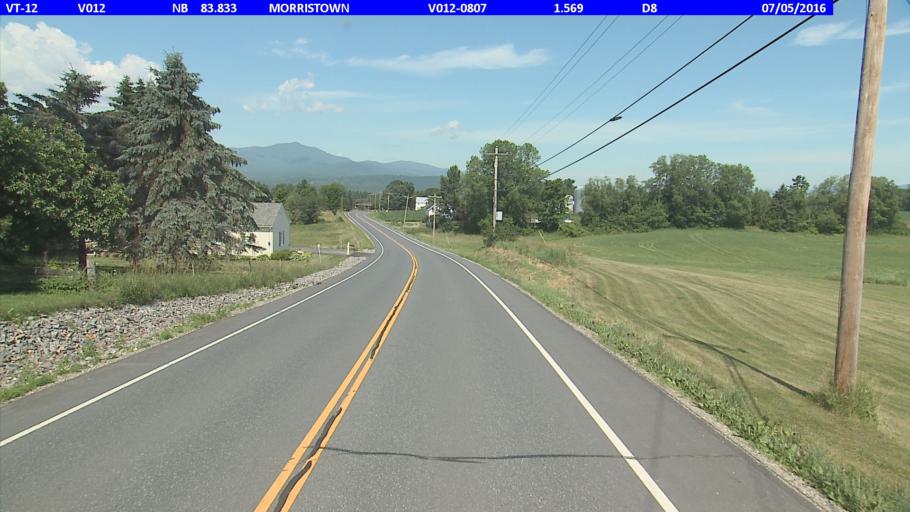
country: US
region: Vermont
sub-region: Lamoille County
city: Morrisville
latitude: 44.5492
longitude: -72.5680
